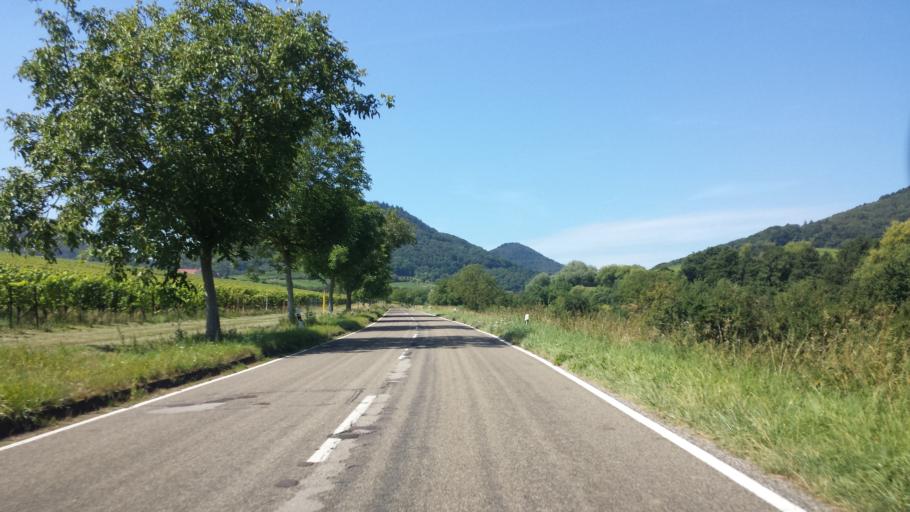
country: DE
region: Rheinland-Pfalz
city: Ranschbach
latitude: 49.1839
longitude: 8.0360
